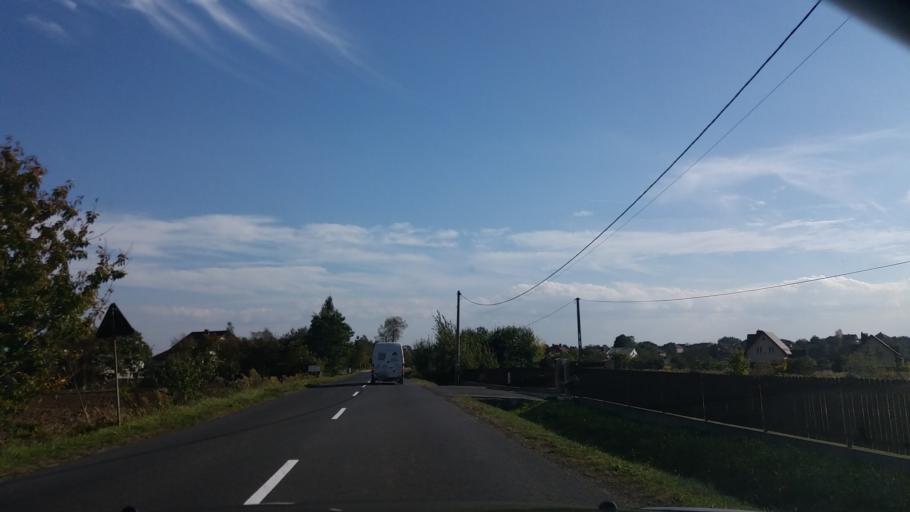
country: PL
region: Lesser Poland Voivodeship
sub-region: Powiat chrzanowski
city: Grojec
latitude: 50.0955
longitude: 19.5547
